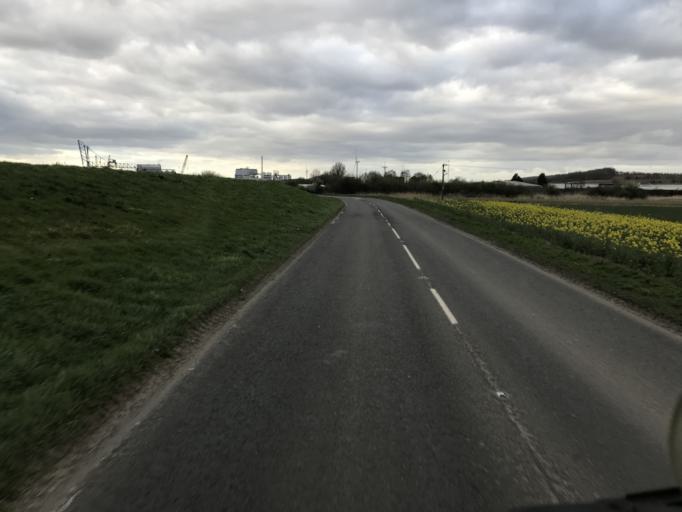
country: GB
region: England
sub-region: North Lincolnshire
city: Burton upon Stather
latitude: 53.6144
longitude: -0.6977
